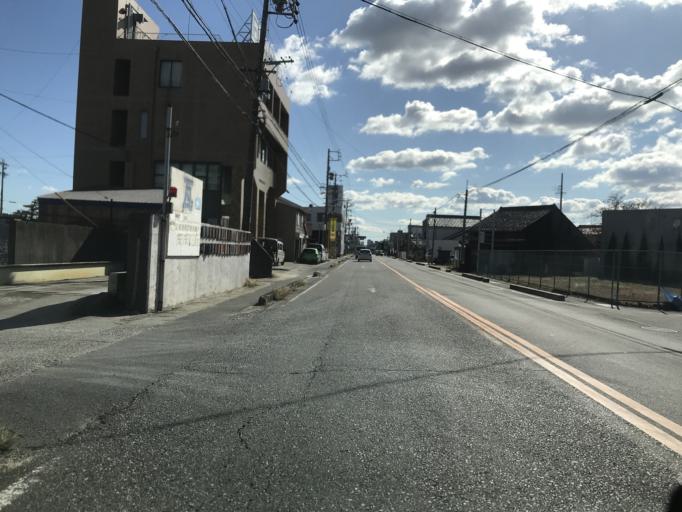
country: JP
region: Aichi
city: Iwakura
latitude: 35.2170
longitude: 136.8461
